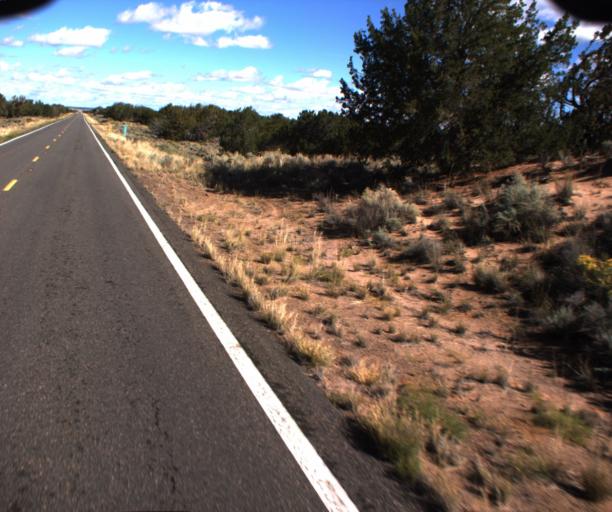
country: US
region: Arizona
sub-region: Apache County
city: Saint Johns
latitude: 34.8642
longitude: -109.2377
